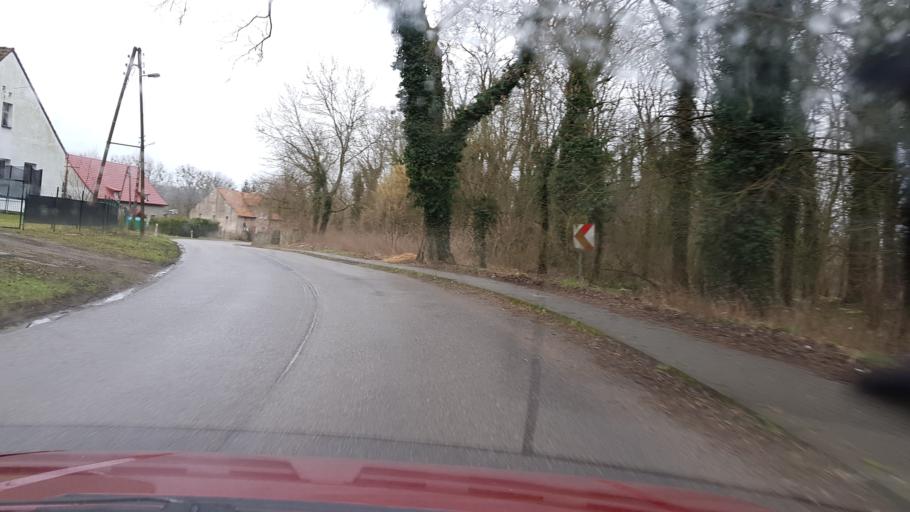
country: PL
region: West Pomeranian Voivodeship
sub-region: Powiat gryfinski
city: Gryfino
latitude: 53.3086
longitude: 14.5950
